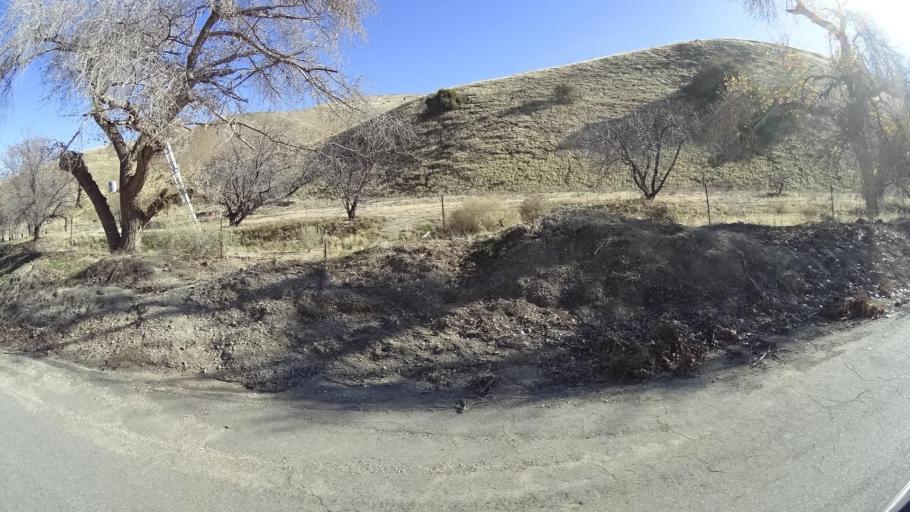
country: US
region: California
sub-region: Kern County
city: Maricopa
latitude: 34.9750
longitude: -119.4095
